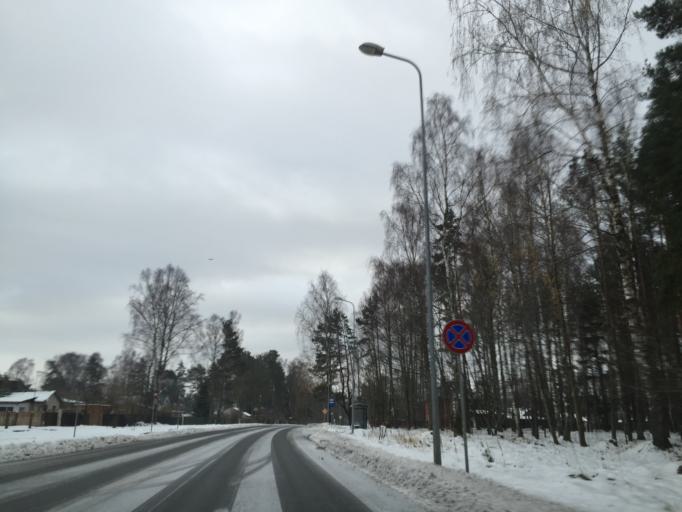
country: LV
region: Saulkrastu
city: Saulkrasti
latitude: 57.2817
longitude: 24.4161
